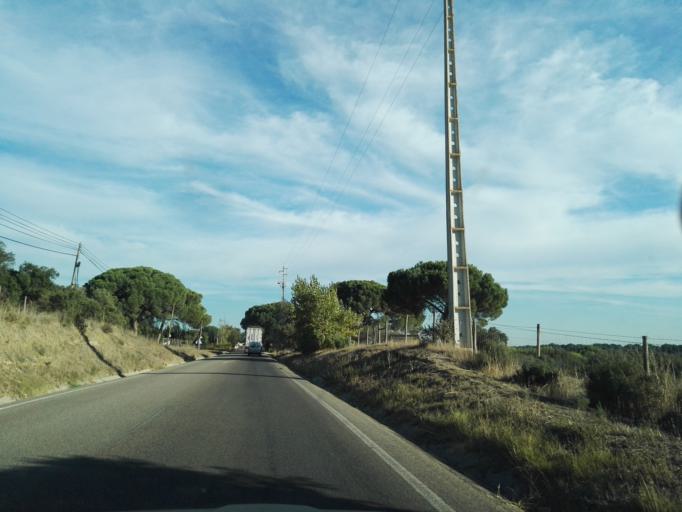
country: PT
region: Santarem
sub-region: Benavente
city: Poceirao
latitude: 38.8510
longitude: -8.7203
